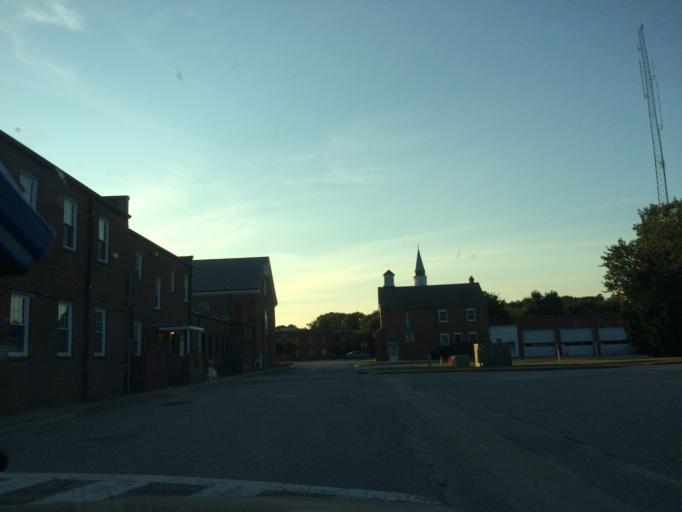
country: US
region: Virginia
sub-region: City of Newport News
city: Newport News
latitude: 37.0322
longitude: -76.4591
